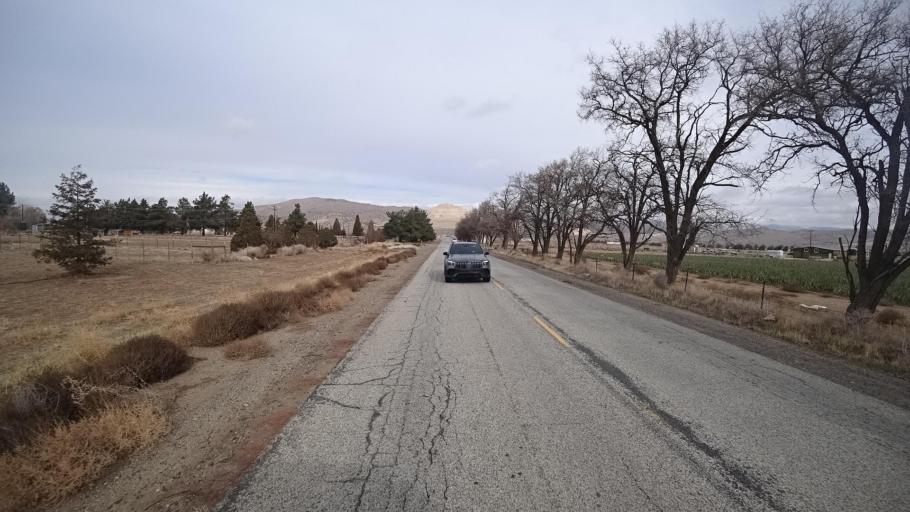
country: US
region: California
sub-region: Kern County
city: Tehachapi
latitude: 35.1161
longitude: -118.3966
